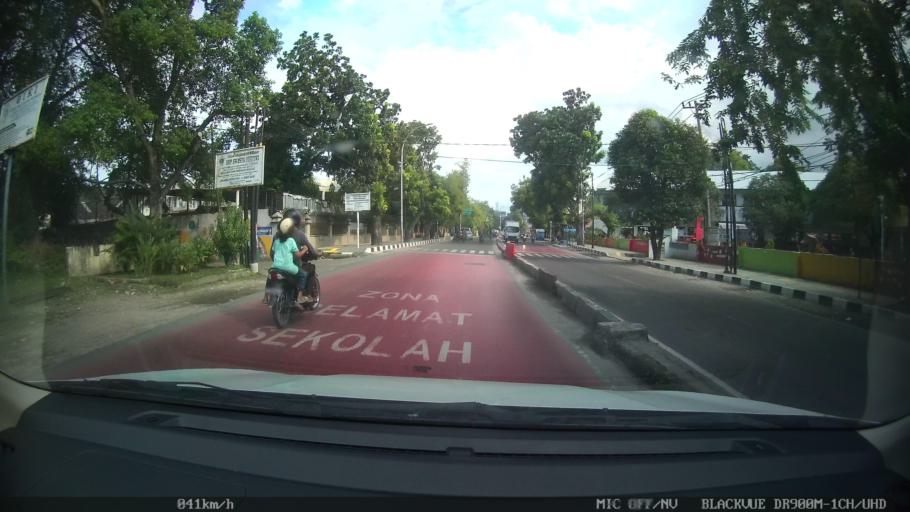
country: ID
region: North Sumatra
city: Medan
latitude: 3.6215
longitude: 98.6705
